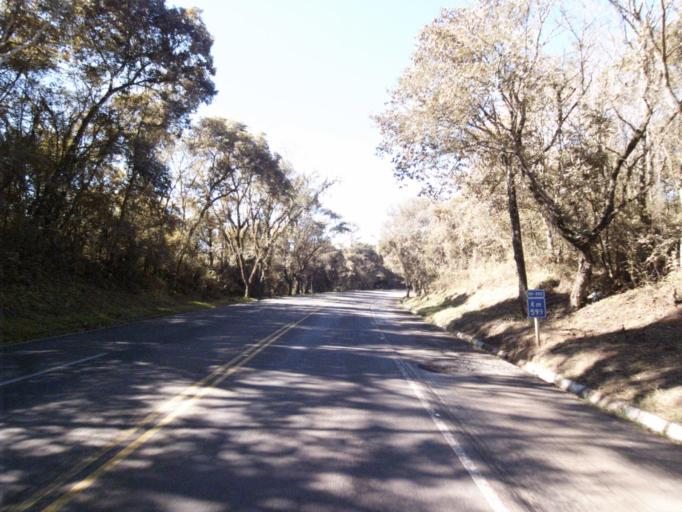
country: BR
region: Santa Catarina
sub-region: Sao Lourenco Do Oeste
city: Sao Lourenco dOeste
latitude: -26.8178
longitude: -53.1595
